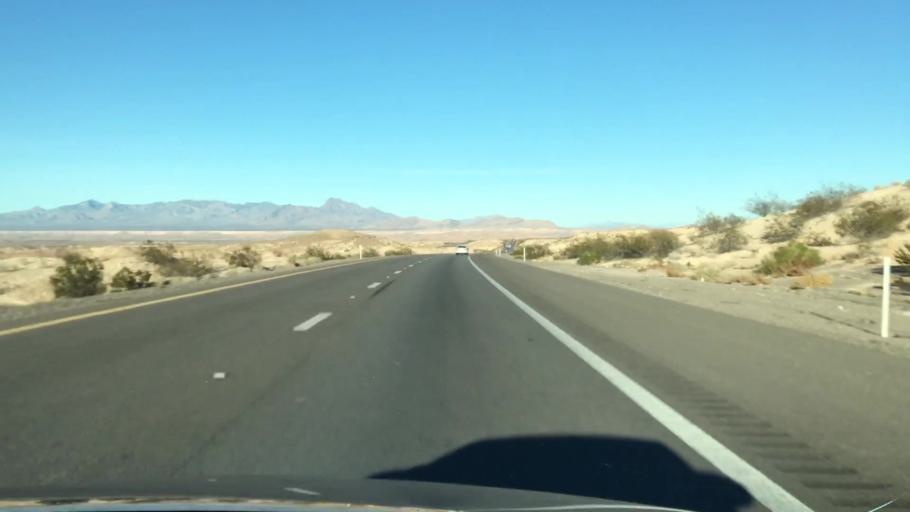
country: US
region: Nevada
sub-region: Clark County
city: Moapa Town
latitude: 36.6005
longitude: -114.6395
